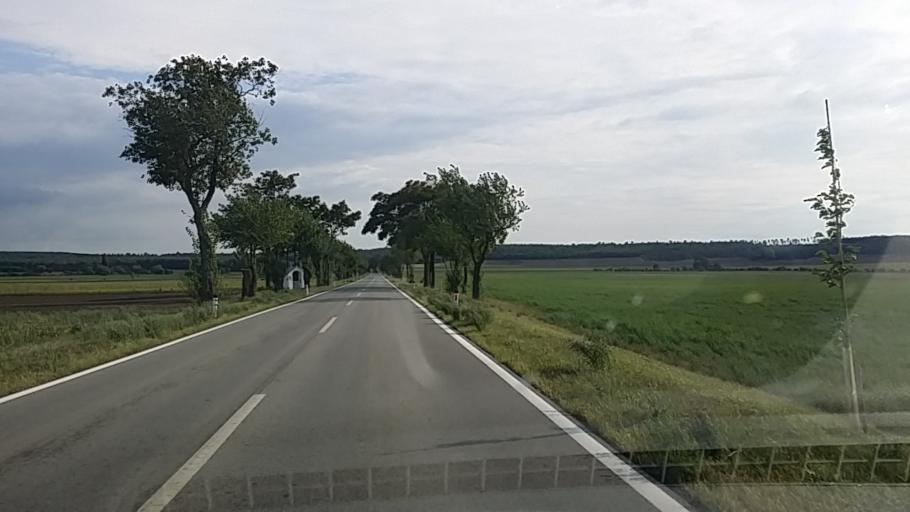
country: AT
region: Burgenland
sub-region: Eisenstadt-Umgebung
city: Sankt Margarethen im Burgenland
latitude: 47.7850
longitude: 16.6170
